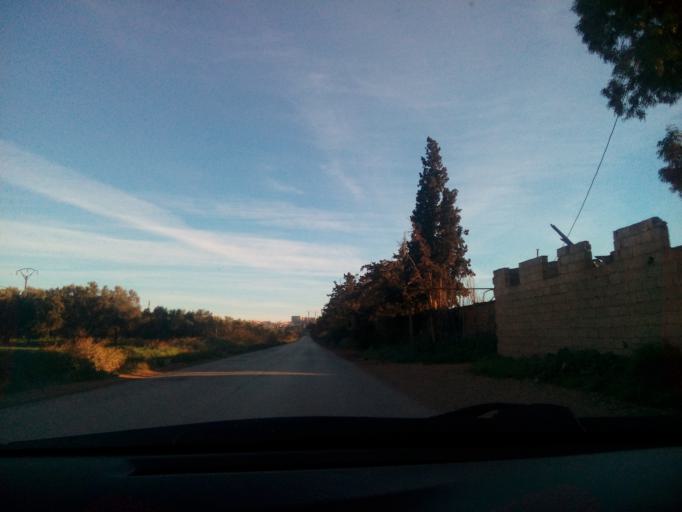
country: DZ
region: Oran
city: Es Senia
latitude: 35.6187
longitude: -0.6827
